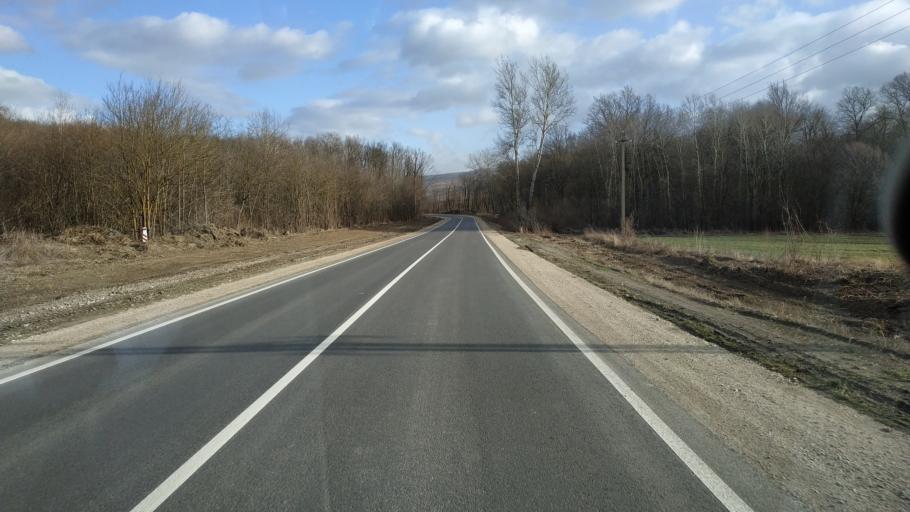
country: MD
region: Calarasi
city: Calarasi
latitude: 47.3053
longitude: 28.1364
